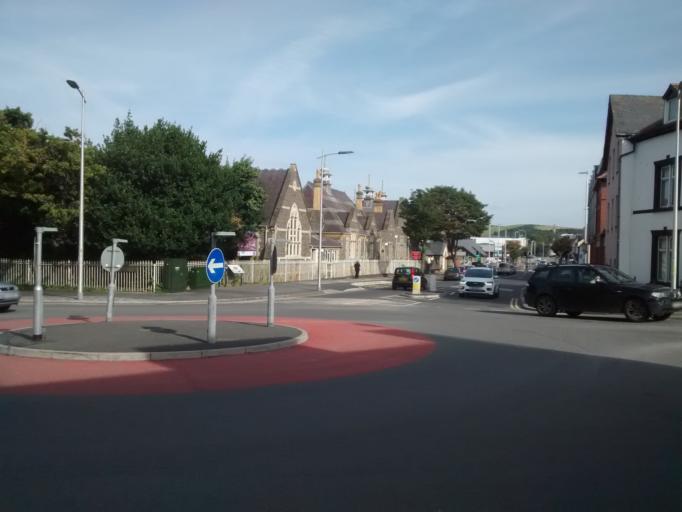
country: GB
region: Wales
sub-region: County of Ceredigion
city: Aberystwyth
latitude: 52.4137
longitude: -4.0833
